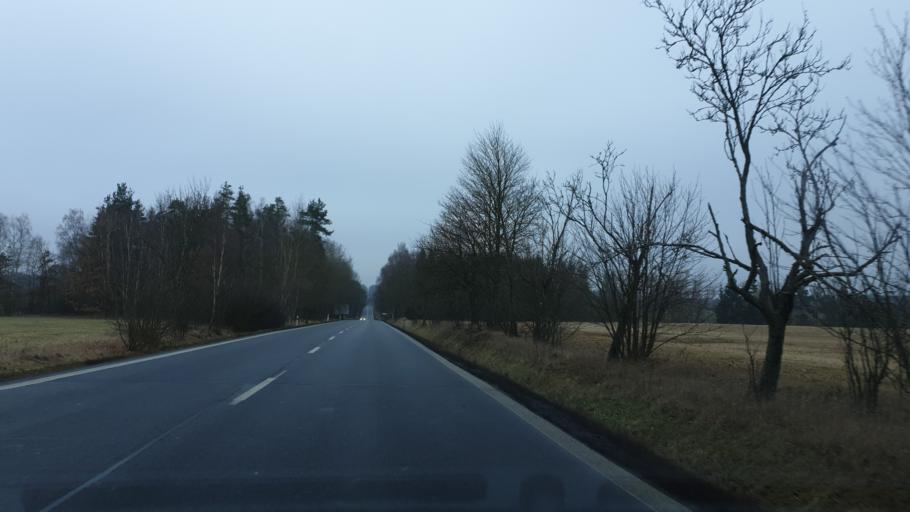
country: CZ
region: Karlovarsky
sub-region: Okres Cheb
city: Frantiskovy Lazne
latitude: 50.1358
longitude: 12.3381
